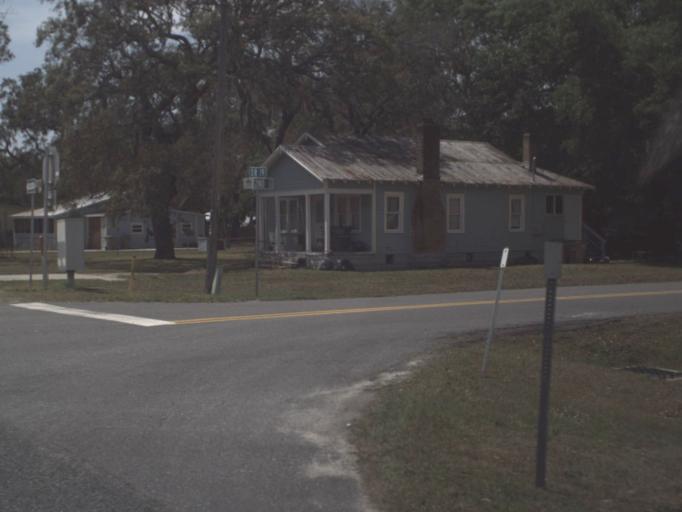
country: US
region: Florida
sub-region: Lake County
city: Umatilla
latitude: 28.8965
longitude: -81.6872
